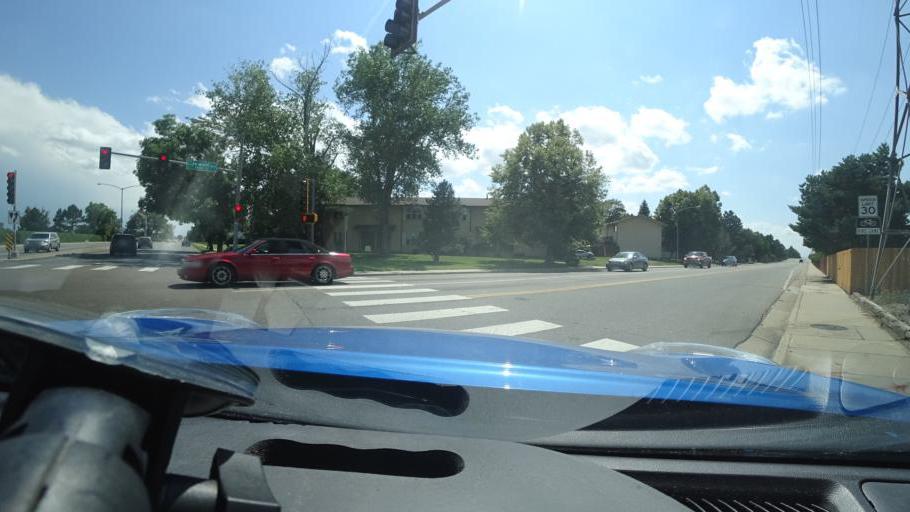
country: US
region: Colorado
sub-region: Adams County
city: Aurora
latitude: 39.6822
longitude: -104.8473
